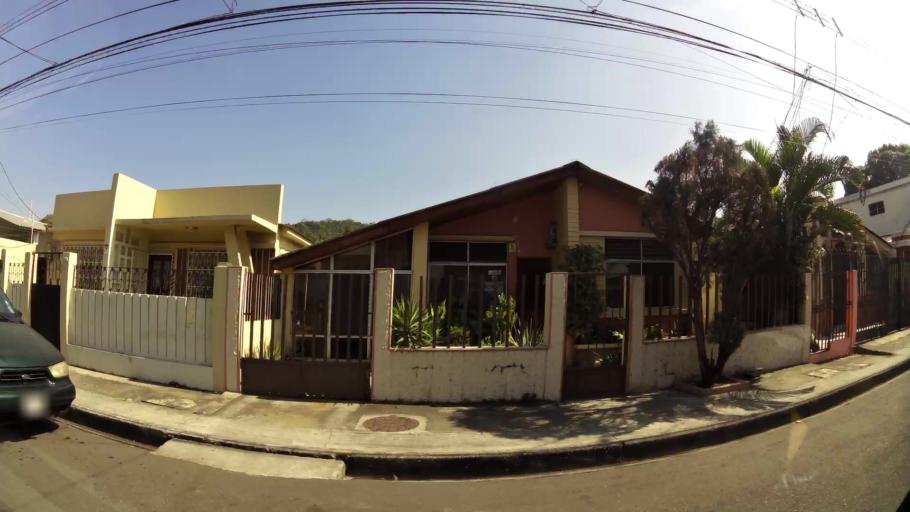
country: EC
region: Guayas
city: Guayaquil
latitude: -2.1657
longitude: -79.9187
